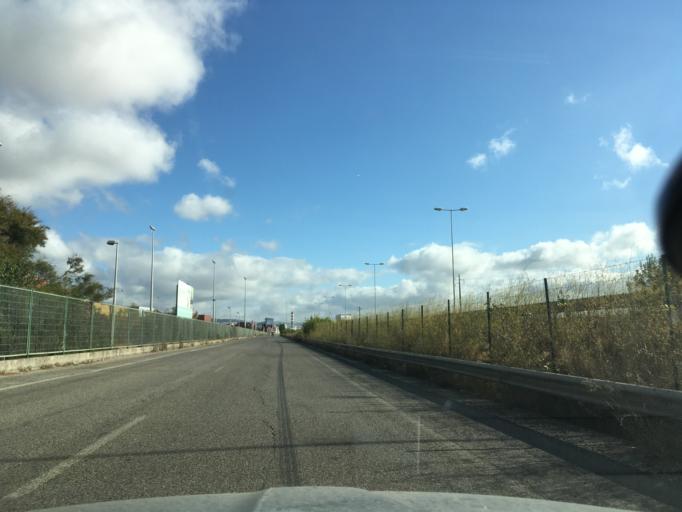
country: PT
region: Lisbon
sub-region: Loures
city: Sao Joao da Talha
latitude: 38.8115
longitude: -9.0893
